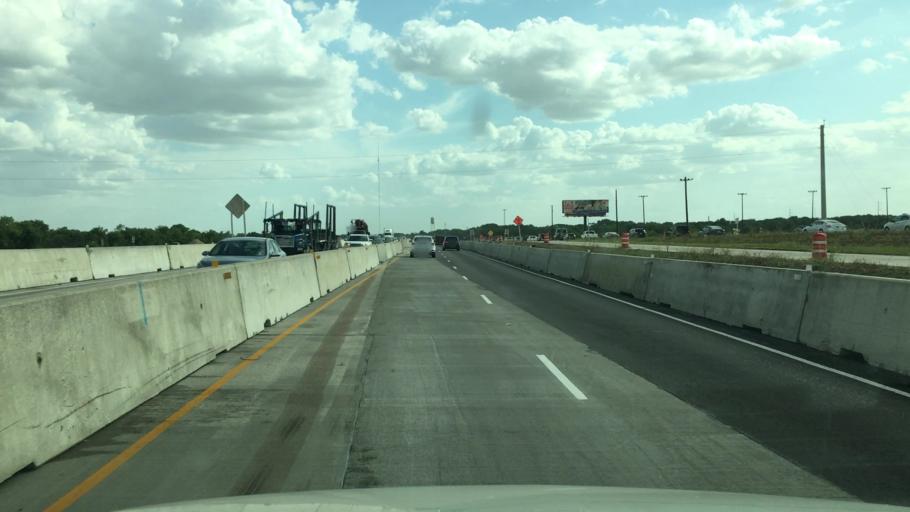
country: US
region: Texas
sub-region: McLennan County
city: Bruceville-Eddy
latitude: 31.3031
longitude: -97.2475
